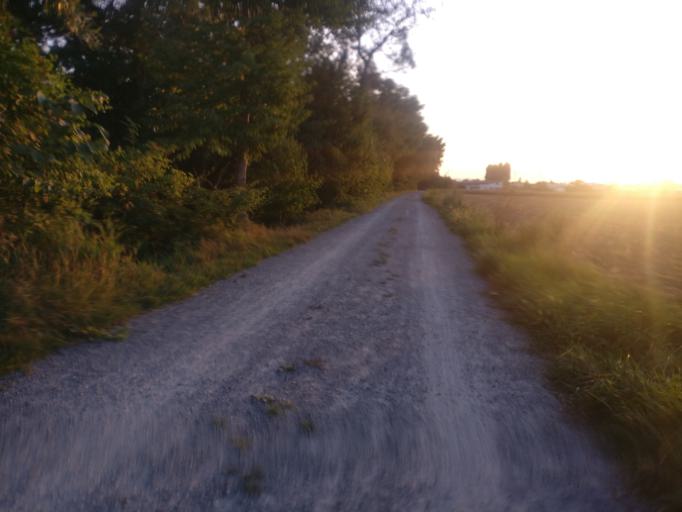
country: AT
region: Lower Austria
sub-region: Politischer Bezirk Baden
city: Ebreichsdorf
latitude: 47.9575
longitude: 16.4191
